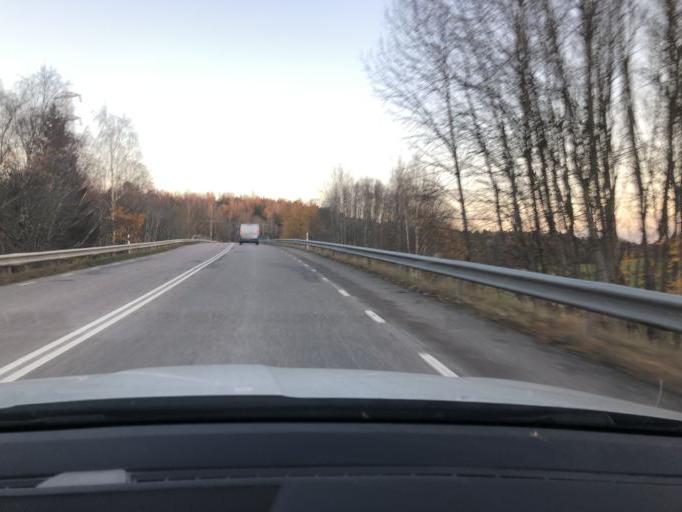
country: SE
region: Soedermanland
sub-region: Strangnas Kommun
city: Akers Styckebruk
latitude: 59.3090
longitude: 17.0876
